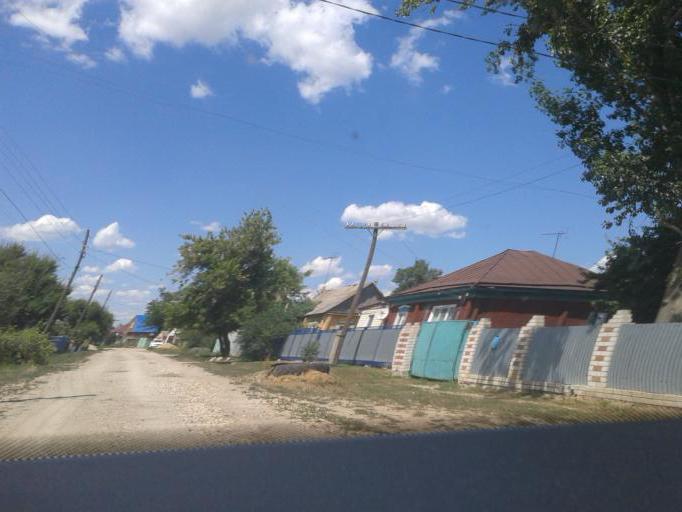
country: RU
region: Volgograd
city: Frolovo
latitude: 49.7622
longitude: 43.6616
